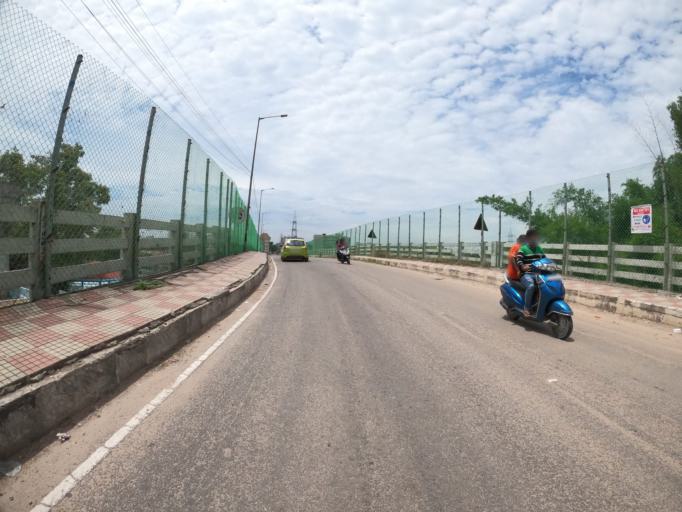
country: IN
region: Telangana
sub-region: Hyderabad
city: Hyderabad
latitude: 17.3725
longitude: 78.4117
